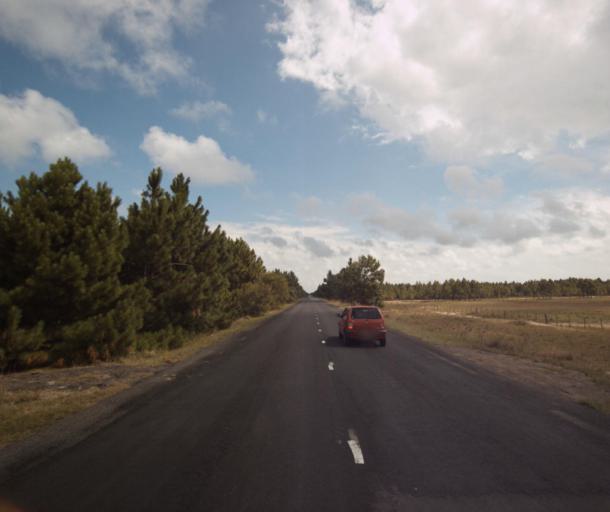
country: BR
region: Rio Grande do Sul
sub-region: Tapes
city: Tapes
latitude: -31.4132
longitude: -51.1712
